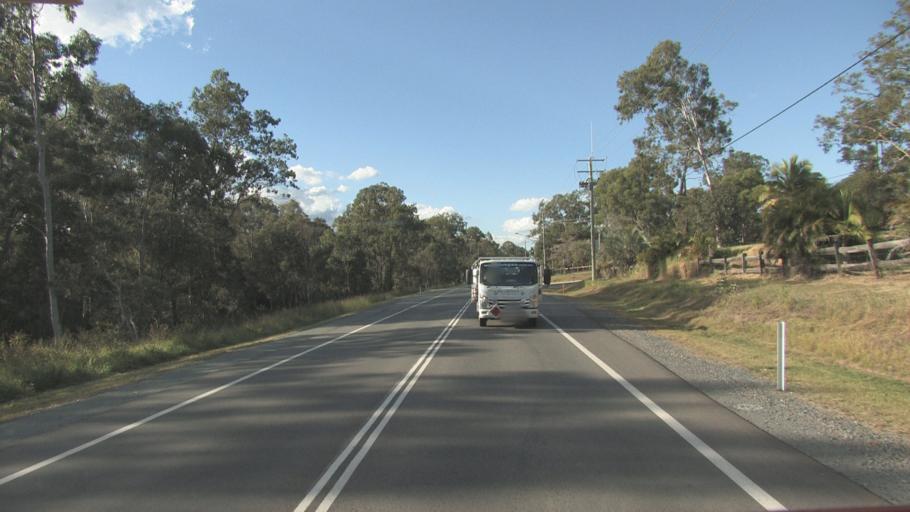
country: AU
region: Queensland
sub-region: Ipswich
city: Springfield Lakes
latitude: -27.7248
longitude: 152.9576
